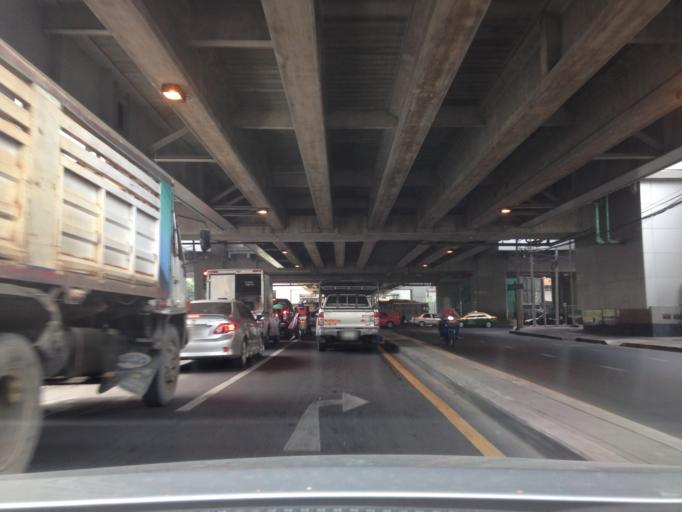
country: TH
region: Bangkok
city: Bang Sue
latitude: 13.8076
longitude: 100.5310
